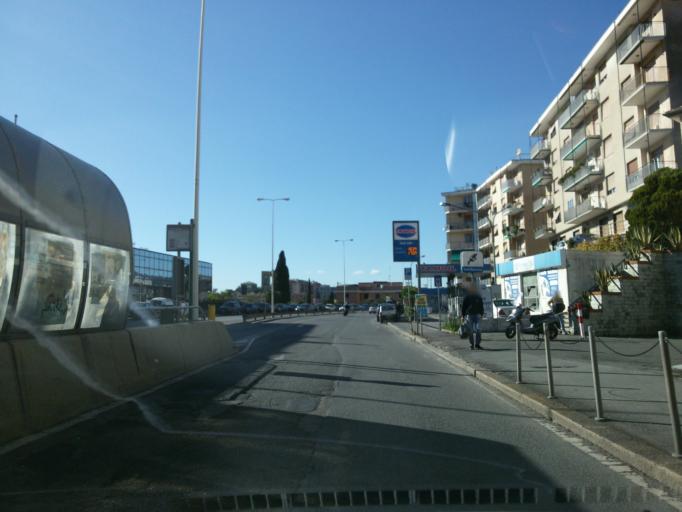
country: IT
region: Liguria
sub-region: Provincia di Genova
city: Bogliasco
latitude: 44.3988
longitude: 8.9916
